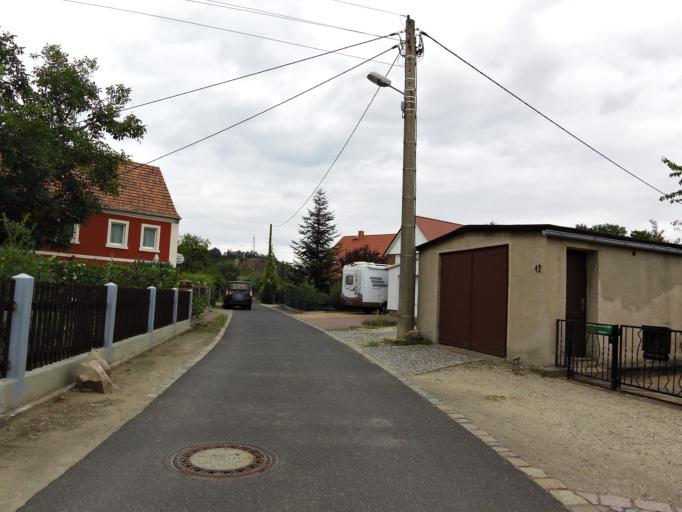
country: DE
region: Saxony
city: Weissig
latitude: 51.2215
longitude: 13.4148
